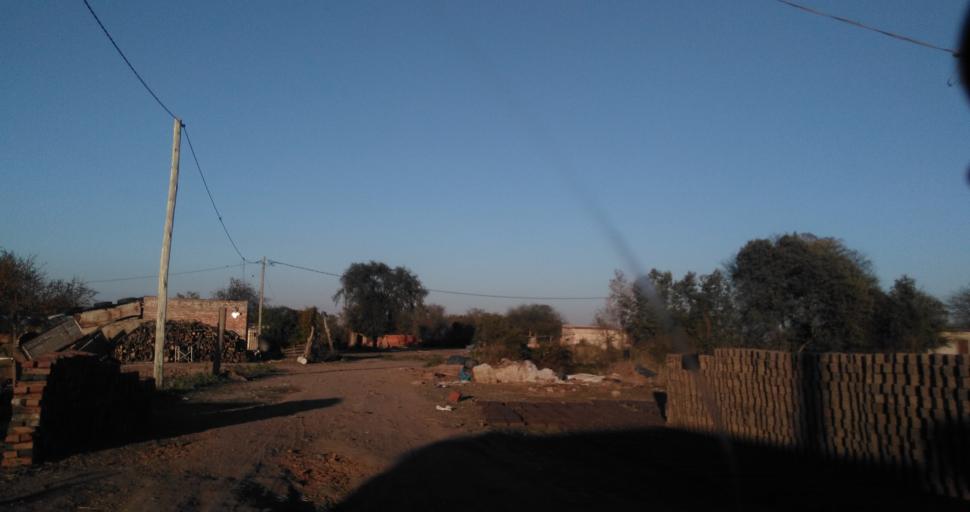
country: AR
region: Chaco
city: Fontana
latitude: -27.4336
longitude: -59.0315
